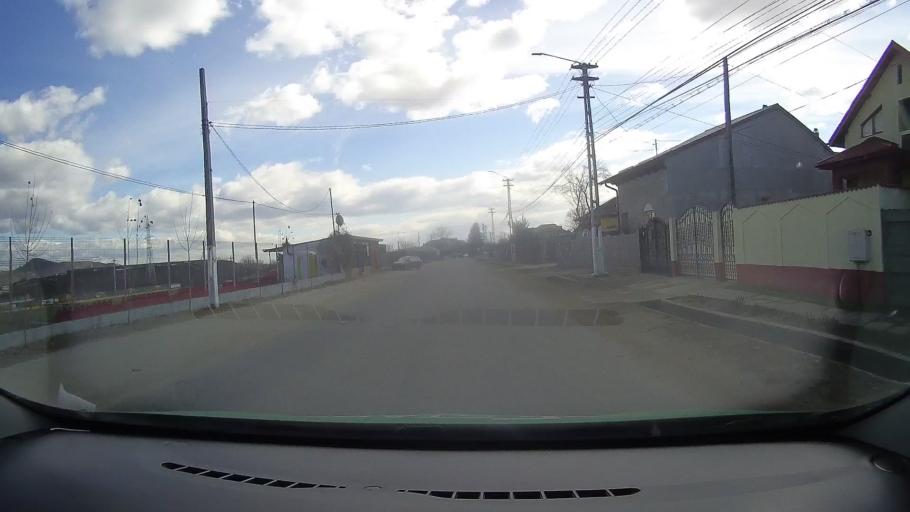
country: RO
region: Dambovita
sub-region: Comuna Doicesti
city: Doicesti
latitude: 44.9856
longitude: 25.3852
